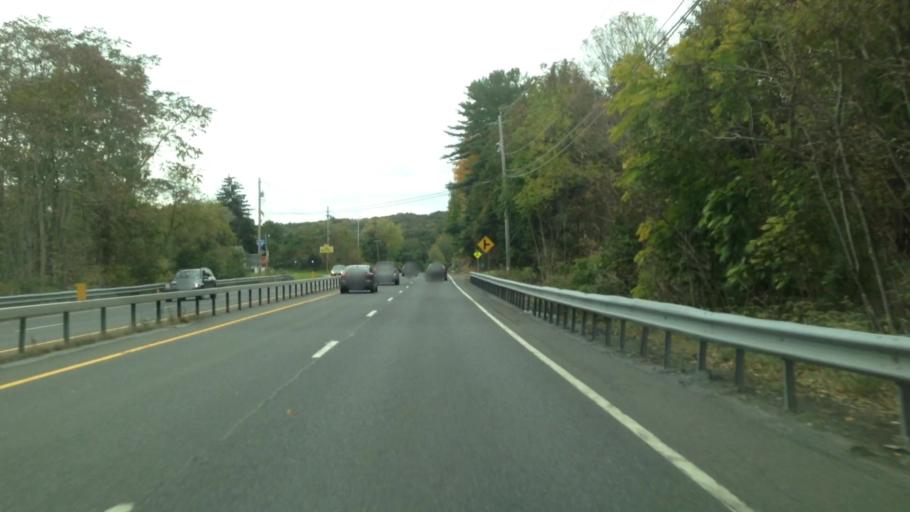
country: US
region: New York
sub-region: Ulster County
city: Highland
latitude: 41.7258
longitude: -73.9614
